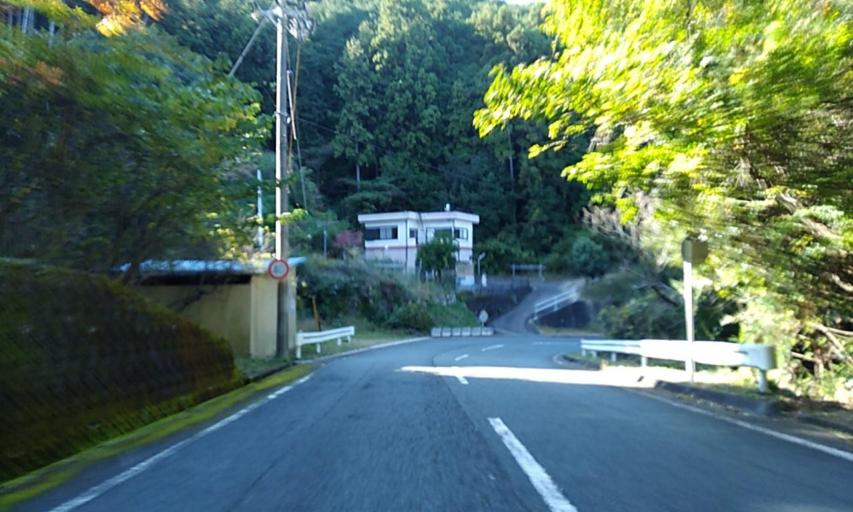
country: JP
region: Shizuoka
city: Hamakita
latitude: 34.8299
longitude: 137.6388
